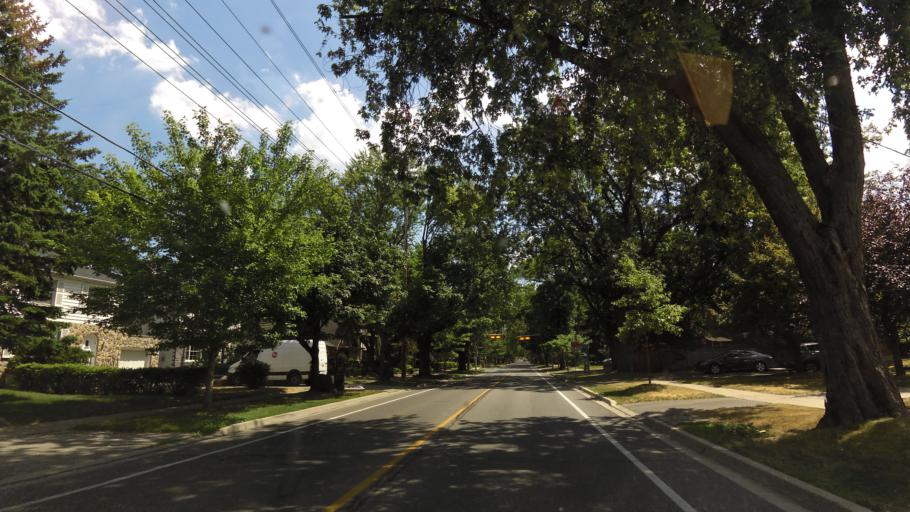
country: CA
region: Ontario
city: Etobicoke
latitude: 43.6544
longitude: -79.5145
